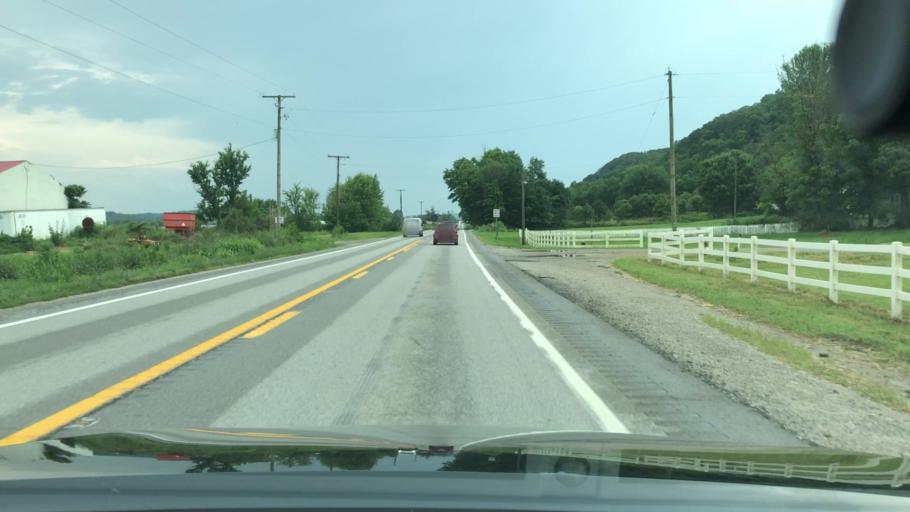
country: US
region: West Virginia
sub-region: Putnam County
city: Buffalo
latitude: 38.7114
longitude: -81.9676
